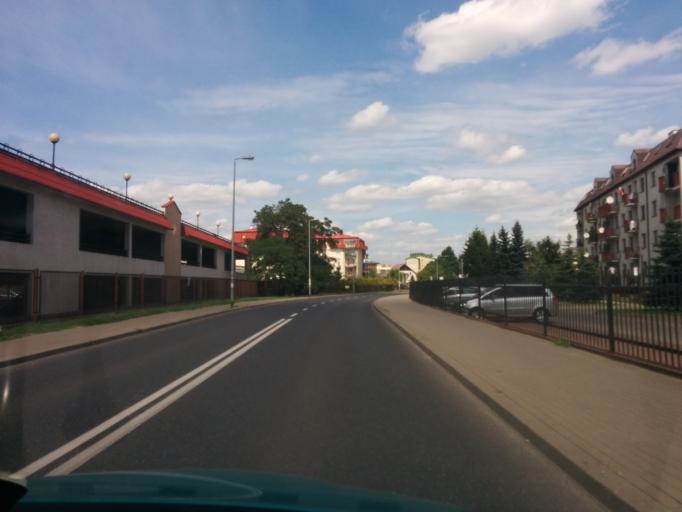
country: PL
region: Masovian Voivodeship
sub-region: Warszawa
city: Bialoleka
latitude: 52.3310
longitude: 20.9358
